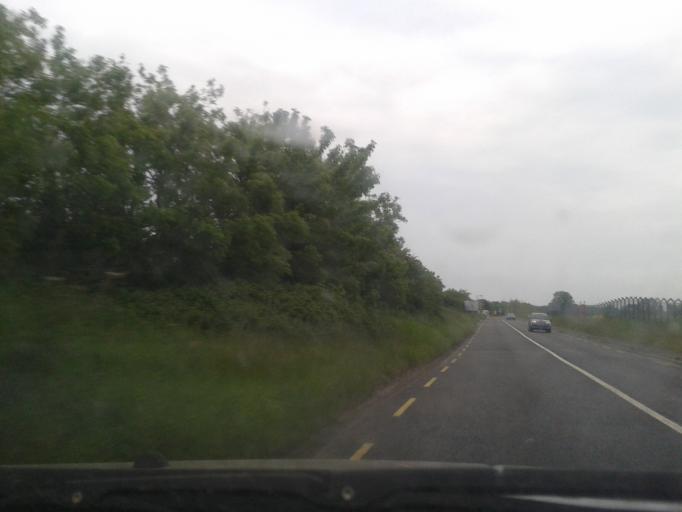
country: IE
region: Leinster
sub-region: Dublin City
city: Finglas
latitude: 53.4222
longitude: -6.3064
